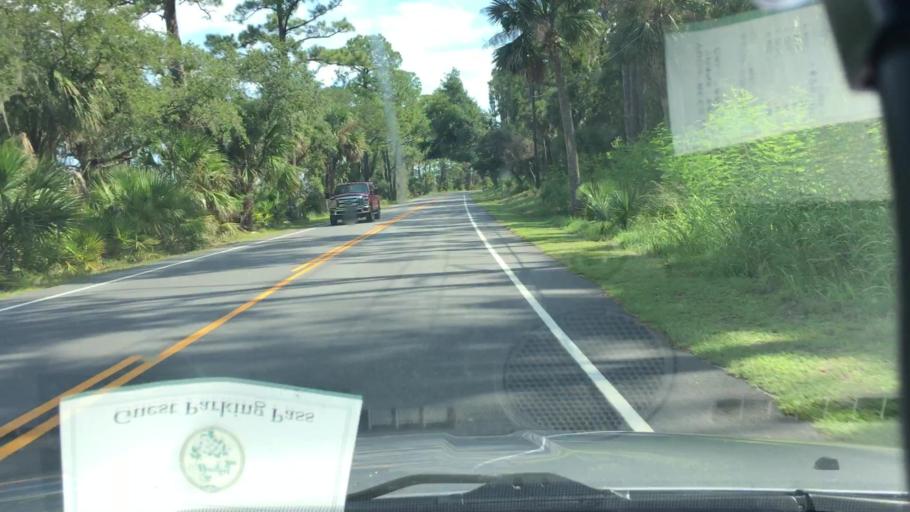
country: US
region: South Carolina
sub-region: Beaufort County
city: Beaufort
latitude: 32.3846
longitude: -80.4415
